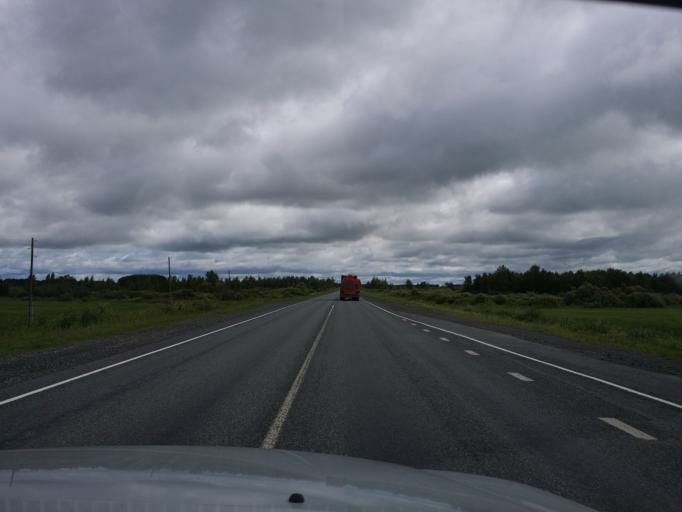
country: RU
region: Tjumen
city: Yarkovo
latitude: 57.2245
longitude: 66.6930
